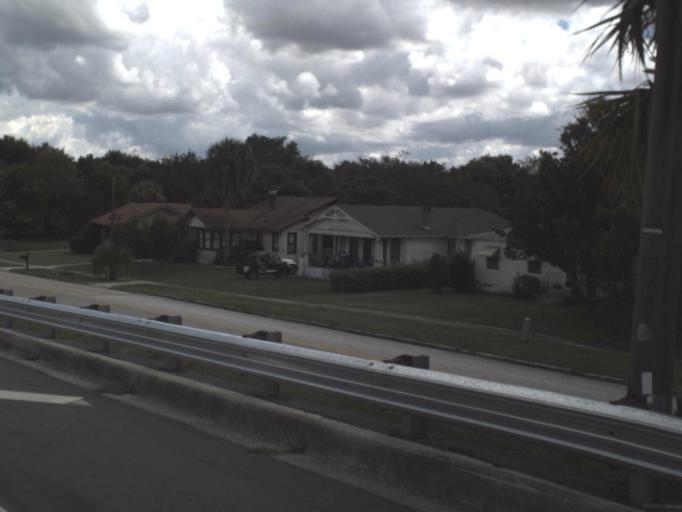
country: US
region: Florida
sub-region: Polk County
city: Lake Wales
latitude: 27.8942
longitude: -81.5793
